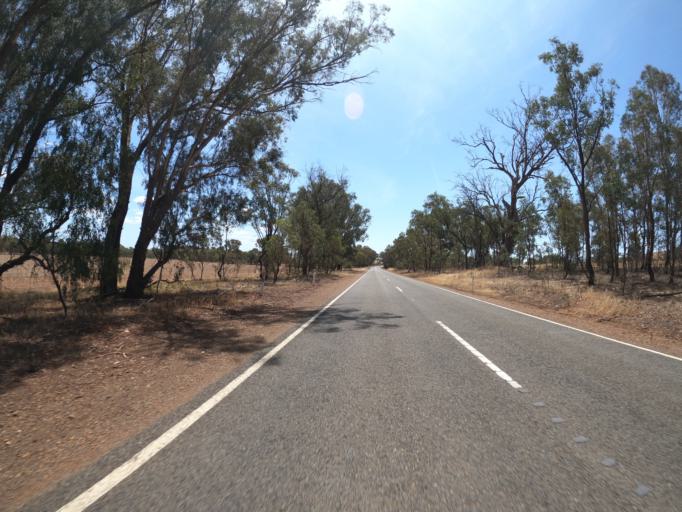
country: AU
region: Victoria
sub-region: Benalla
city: Benalla
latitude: -36.3458
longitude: 145.9604
